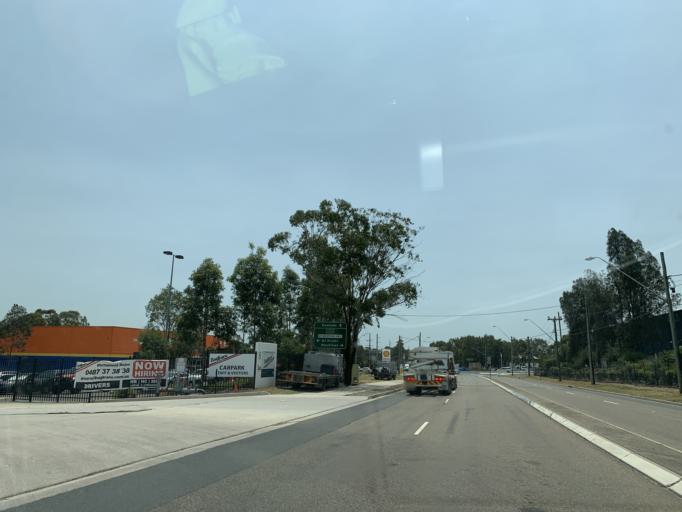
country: AU
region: New South Wales
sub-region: Blacktown
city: Doonside
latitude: -33.7941
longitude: 150.8713
